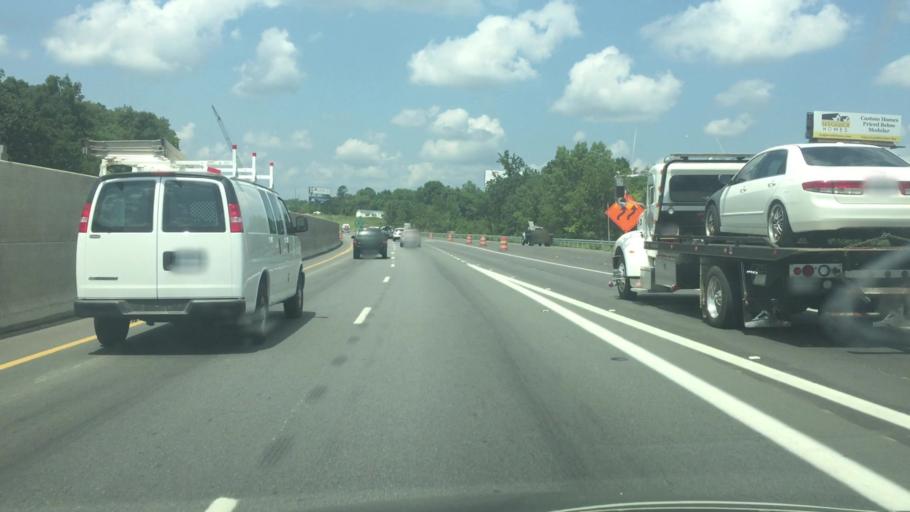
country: US
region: North Carolina
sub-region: Cabarrus County
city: Kannapolis
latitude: 35.5021
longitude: -80.5629
